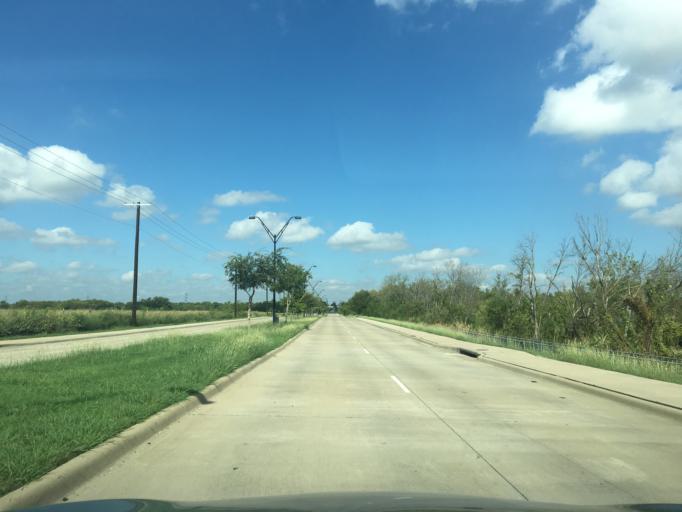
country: US
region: Texas
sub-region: Dallas County
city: Sachse
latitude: 32.9547
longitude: -96.5900
